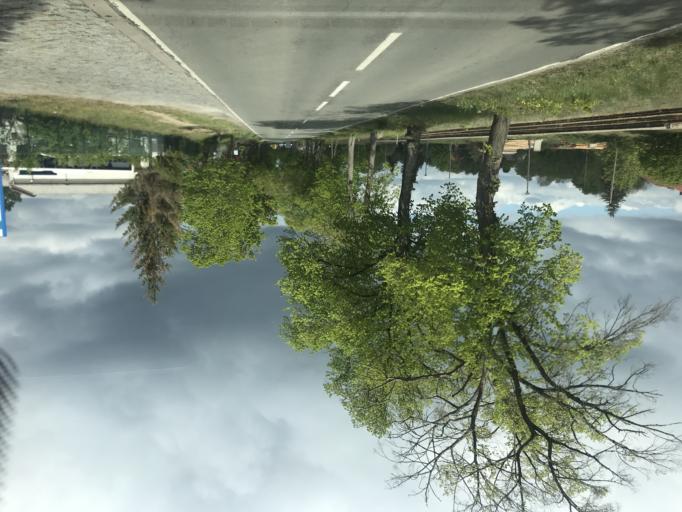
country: DE
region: Brandenburg
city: Rheinsberg
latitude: 53.0901
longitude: 12.9048
